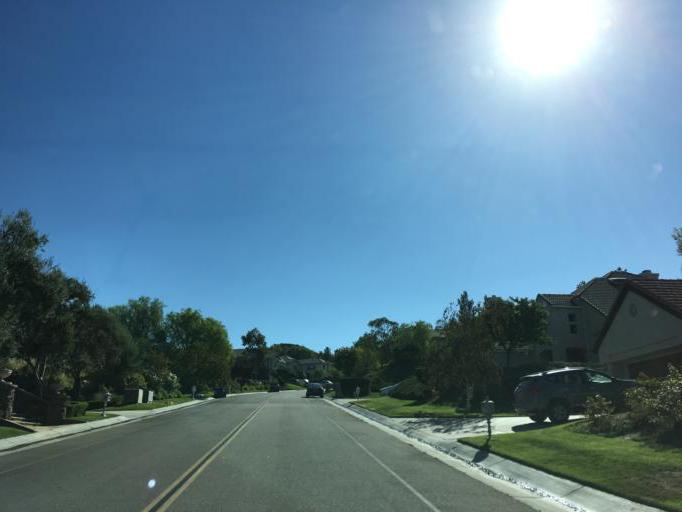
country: US
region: California
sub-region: Los Angeles County
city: Agua Dulce
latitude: 34.4031
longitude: -118.4049
